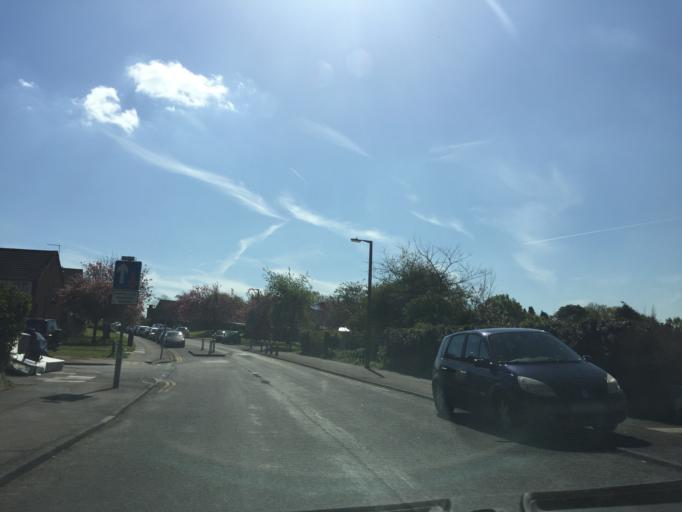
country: GB
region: England
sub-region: Essex
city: Harlow
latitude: 51.7663
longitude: 0.0814
